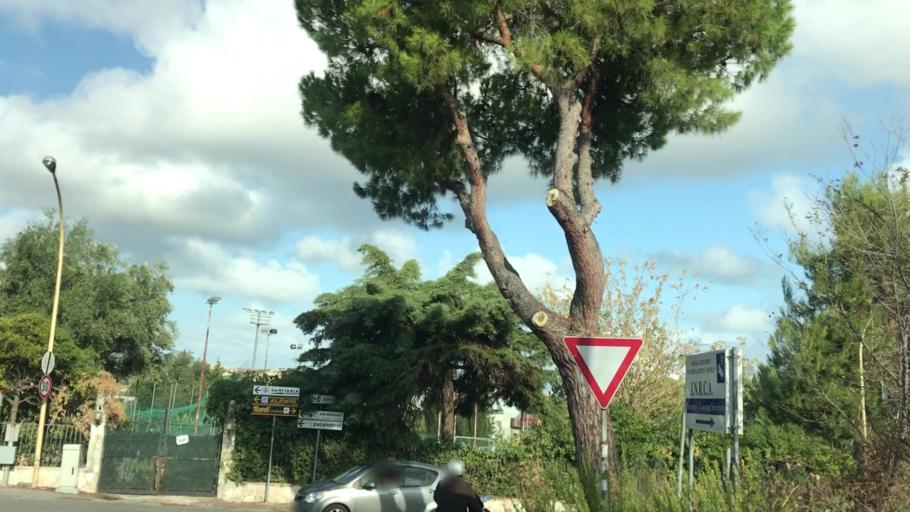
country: IT
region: The Marches
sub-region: Provincia di Ancona
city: Le Grazie di Ancona
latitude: 43.5954
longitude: 13.5131
